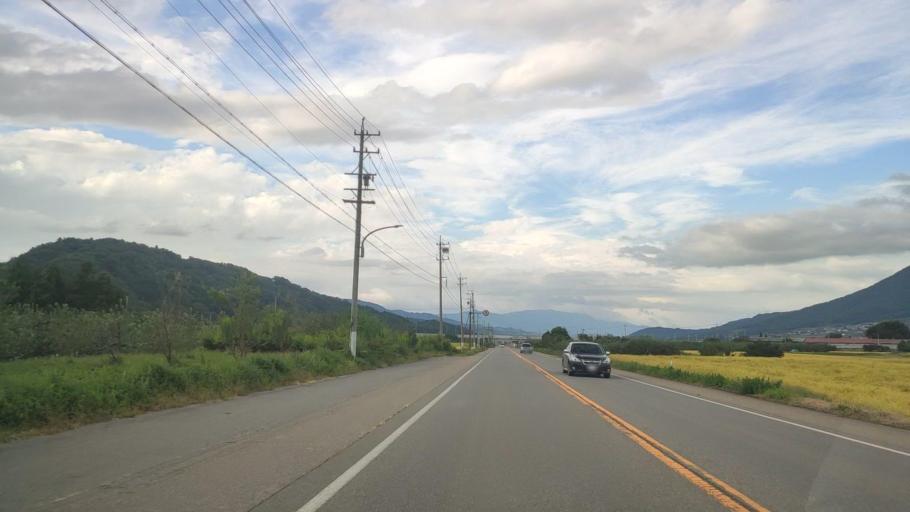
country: JP
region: Nagano
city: Nakano
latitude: 36.7766
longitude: 138.3506
